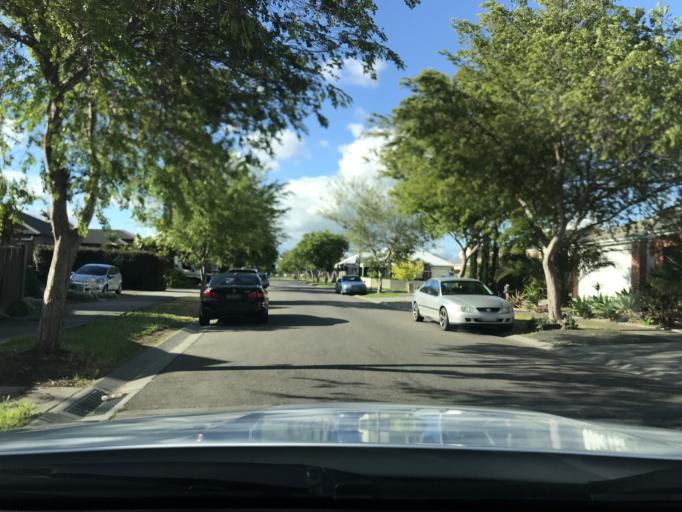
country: AU
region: Victoria
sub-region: Hume
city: Roxburgh Park
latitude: -37.5885
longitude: 144.9034
